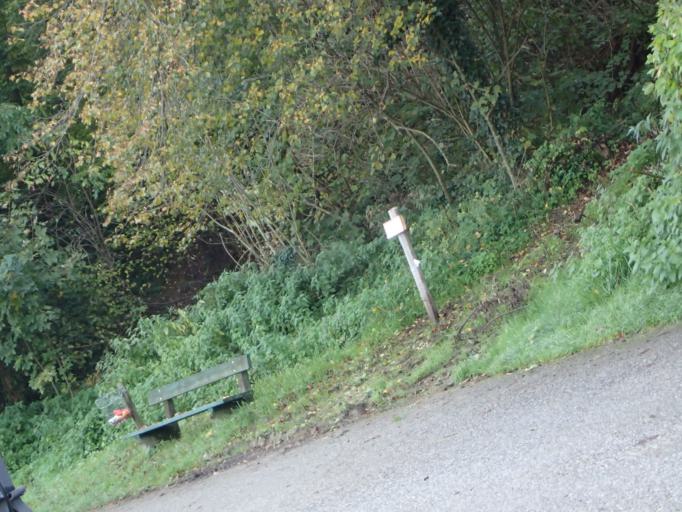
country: AT
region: Salzburg
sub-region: Politischer Bezirk Salzburg-Umgebung
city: Mattsee
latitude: 47.9720
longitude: 13.1006
